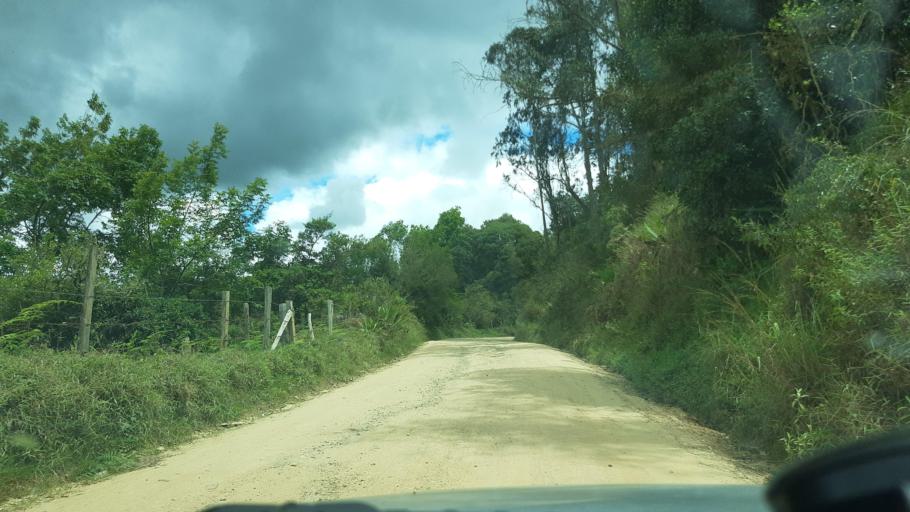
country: CO
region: Cundinamarca
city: Umbita
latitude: 5.2195
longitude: -73.4471
